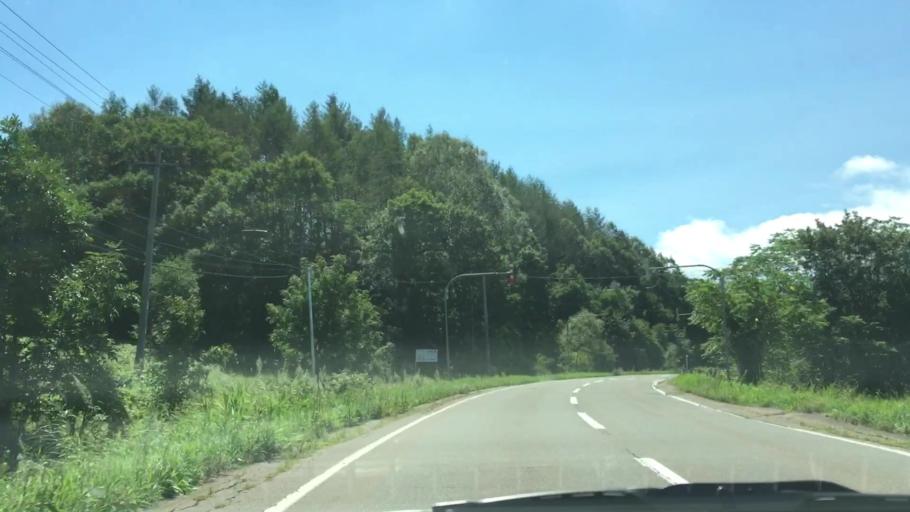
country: JP
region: Hokkaido
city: Kitami
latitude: 43.3173
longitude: 143.7217
